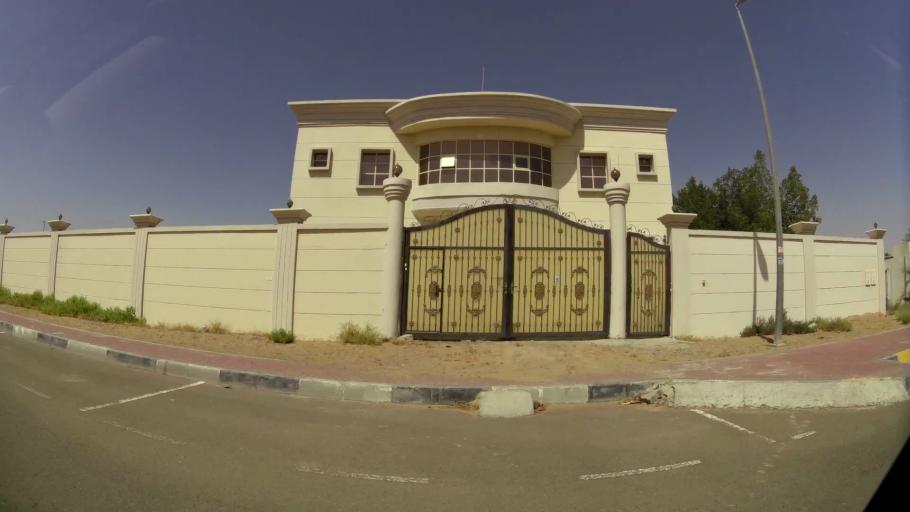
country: OM
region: Al Buraimi
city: Al Buraymi
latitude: 24.3035
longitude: 55.7584
